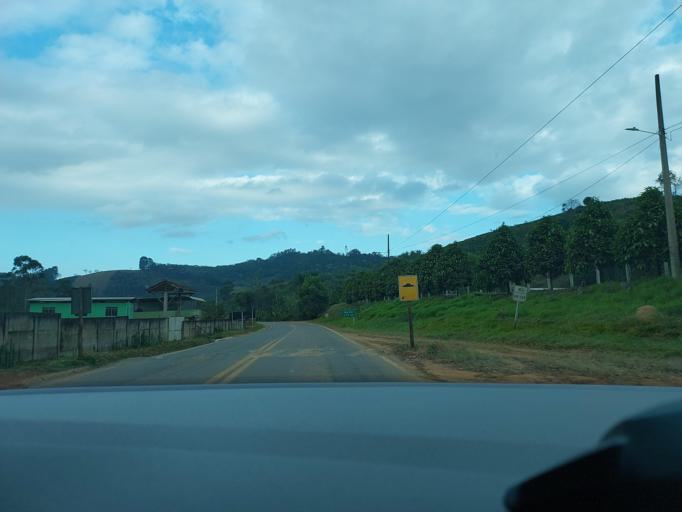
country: BR
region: Minas Gerais
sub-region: Mirai
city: Mirai
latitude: -20.9971
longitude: -42.5543
